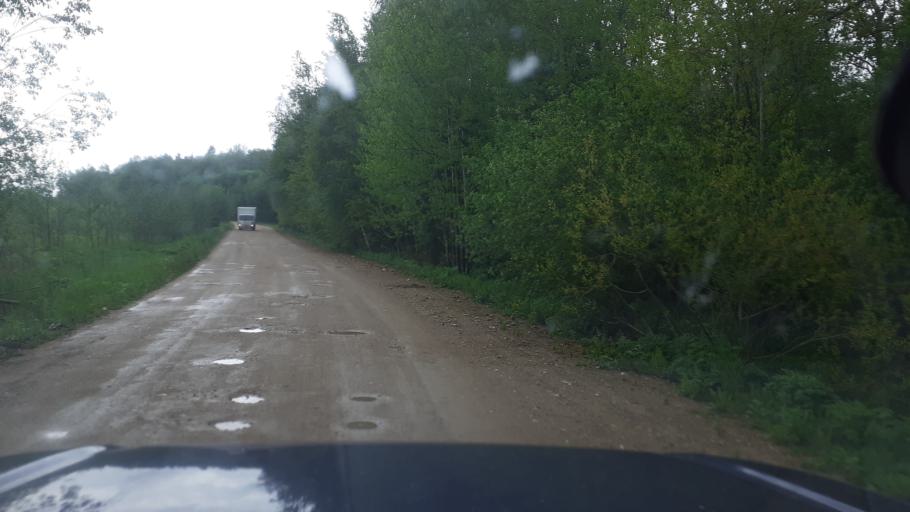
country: RU
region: Moskovskaya
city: Sychevo
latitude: 55.9664
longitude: 36.2626
